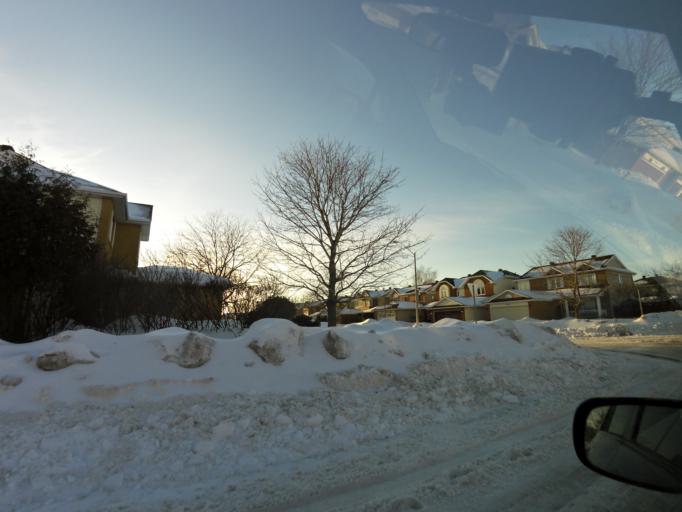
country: CA
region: Ontario
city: Ottawa
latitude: 45.4395
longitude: -75.5244
